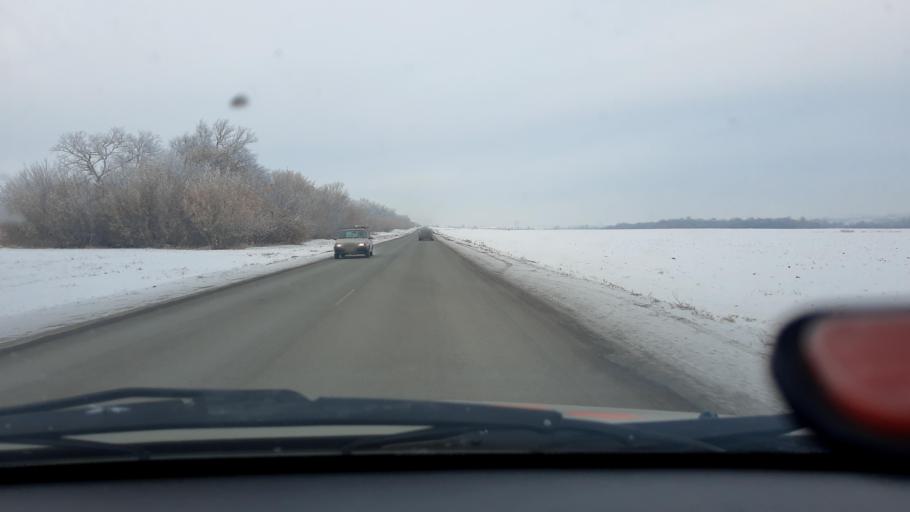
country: RU
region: Bashkortostan
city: Avdon
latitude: 54.3912
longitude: 55.8059
